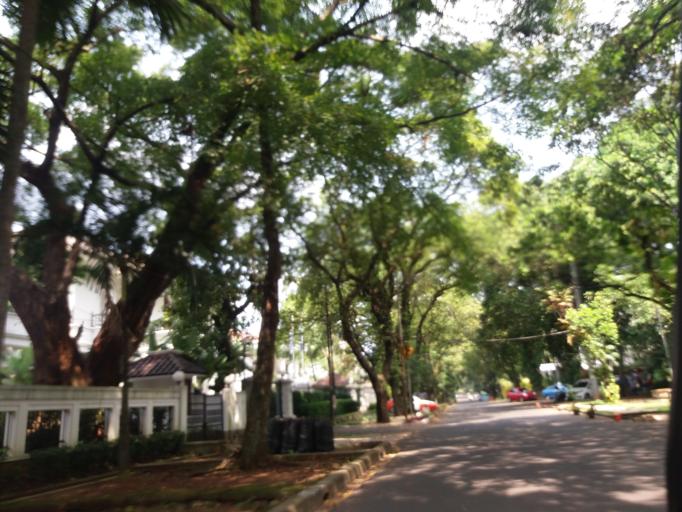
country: ID
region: Jakarta Raya
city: Jakarta
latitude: -6.2338
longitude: 106.8033
